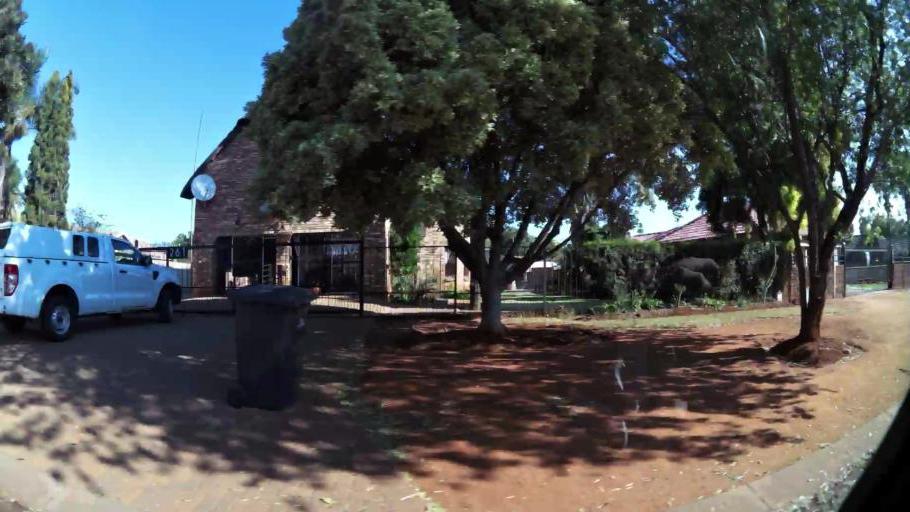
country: ZA
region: North-West
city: Ga-Rankuwa
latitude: -25.6665
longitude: 28.0926
